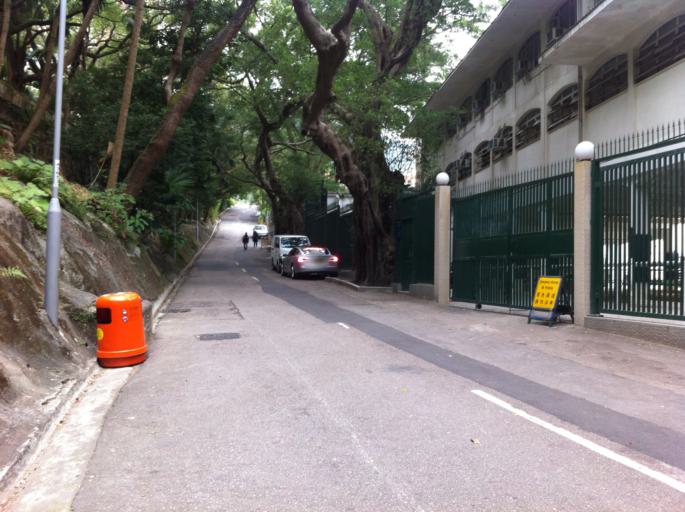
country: HK
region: Central and Western
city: Central
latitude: 22.2633
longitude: 114.1356
